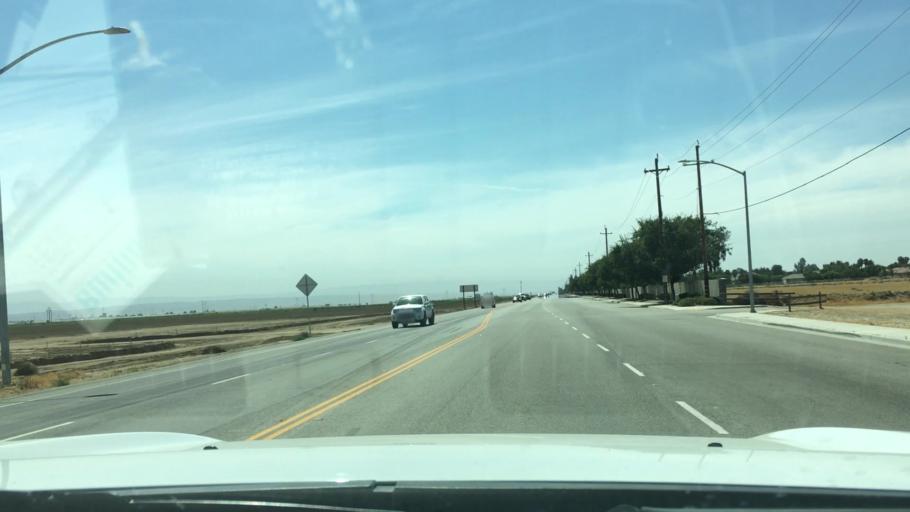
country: US
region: California
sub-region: Kern County
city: Rosedale
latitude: 35.3545
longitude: -119.1825
